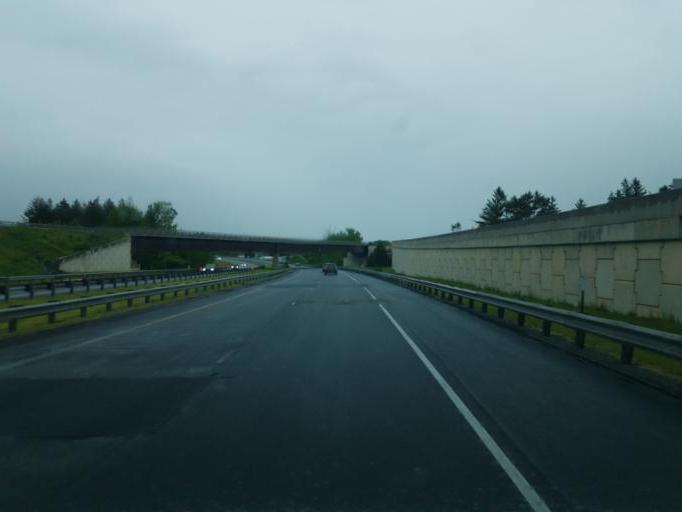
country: US
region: New York
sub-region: Oneida County
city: Yorkville
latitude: 43.1358
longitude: -75.2686
